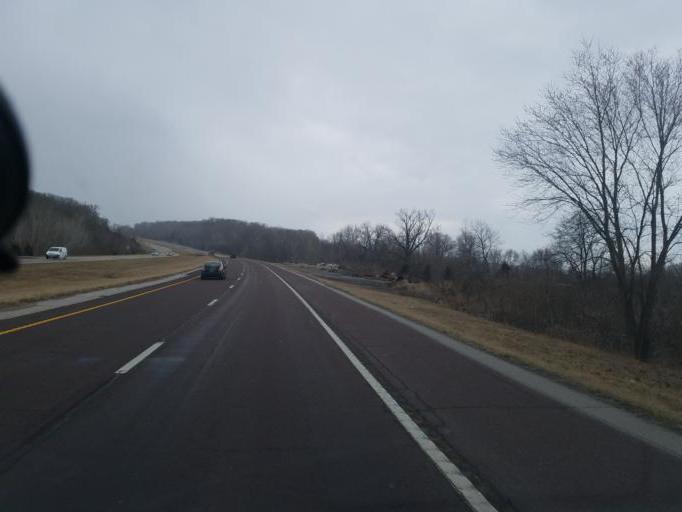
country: US
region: Missouri
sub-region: Boone County
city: Hallsville
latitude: 39.1282
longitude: -92.3332
